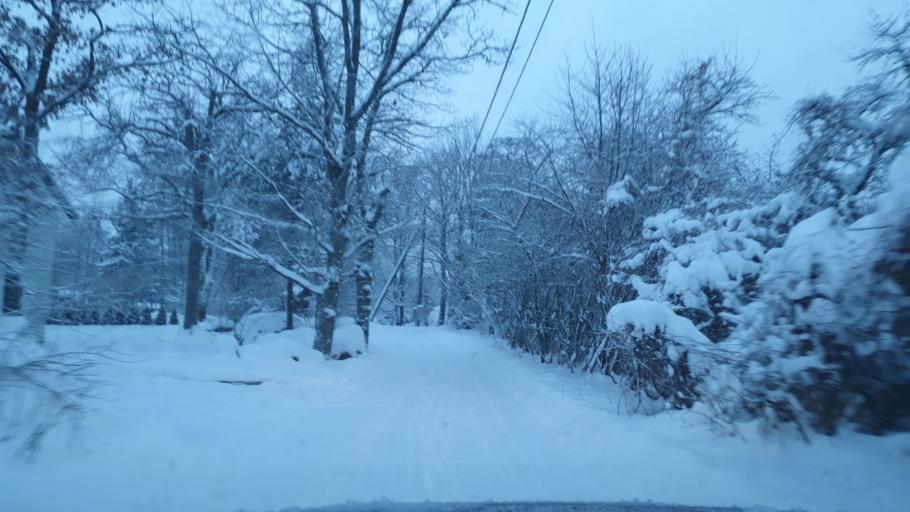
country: EE
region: Harju
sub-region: Viimsi vald
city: Viimsi
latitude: 59.5165
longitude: 24.9096
